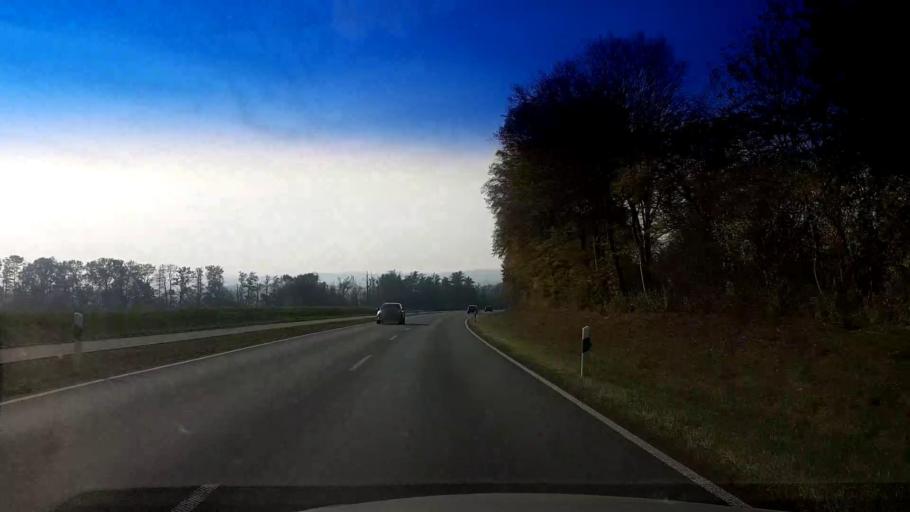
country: DE
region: Bavaria
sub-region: Upper Franconia
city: Himmelkron
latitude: 50.0741
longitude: 11.6095
